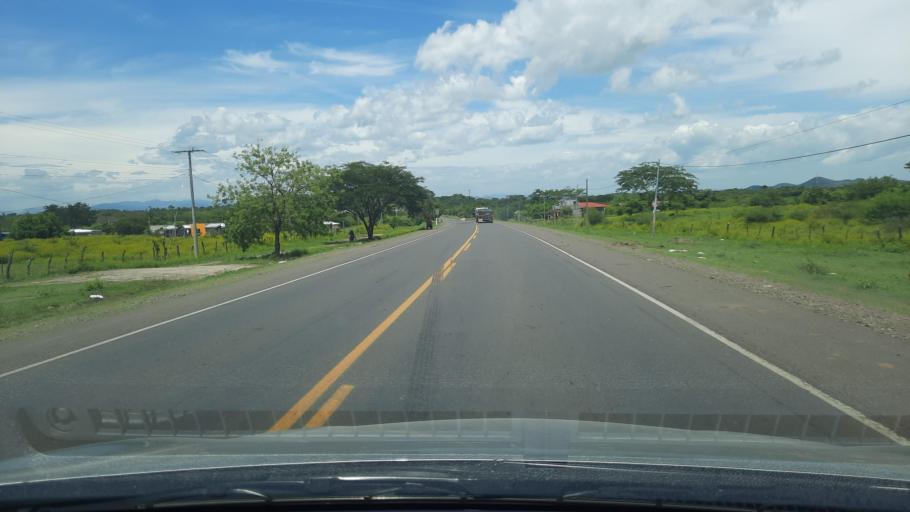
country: NI
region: Chinandega
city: Somotillo
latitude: 13.0561
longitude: -86.9220
